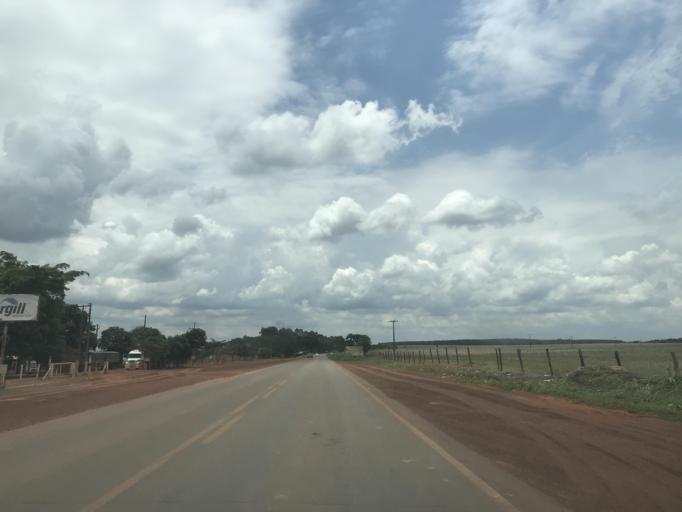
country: BR
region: Goias
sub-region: Vianopolis
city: Vianopolis
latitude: -16.7426
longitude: -48.4685
